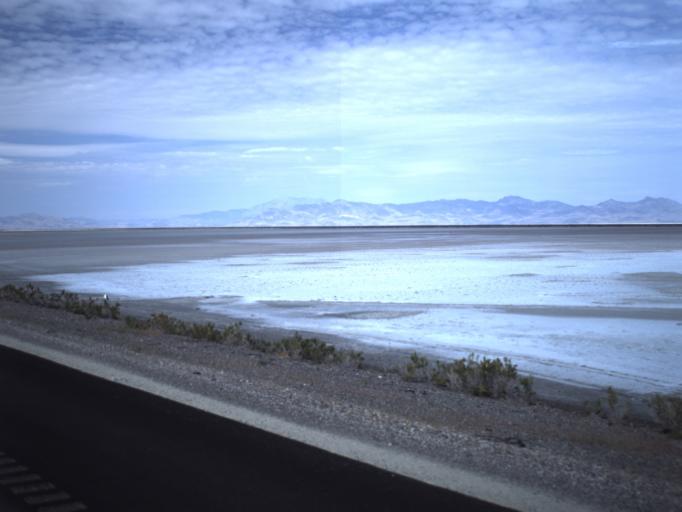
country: US
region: Utah
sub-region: Tooele County
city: Wendover
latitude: 40.7328
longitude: -113.5429
